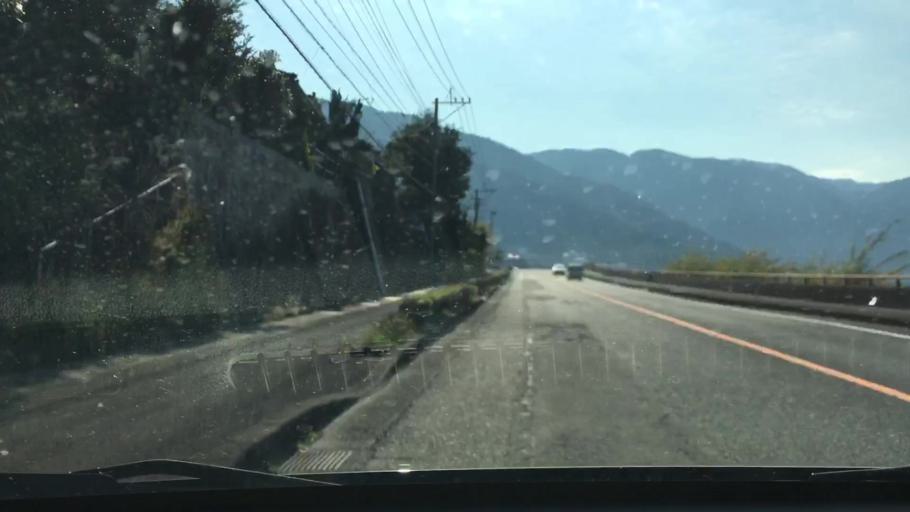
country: JP
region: Kagoshima
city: Kokubu-matsuki
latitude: 31.6645
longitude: 130.8204
